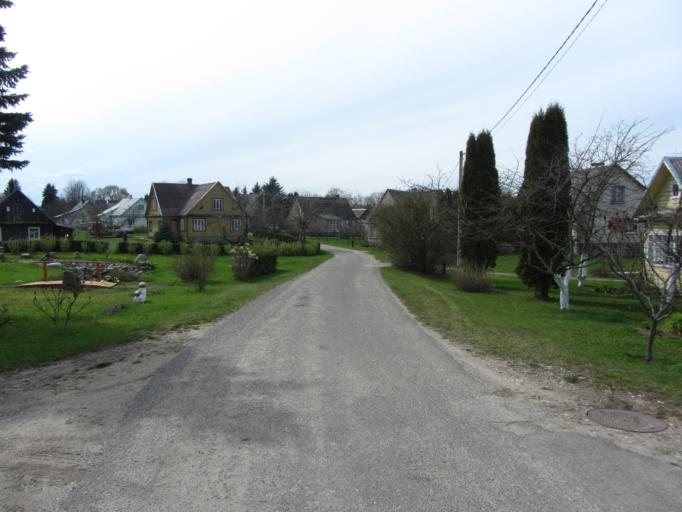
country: LT
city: Zarasai
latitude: 55.5760
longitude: 26.1436
